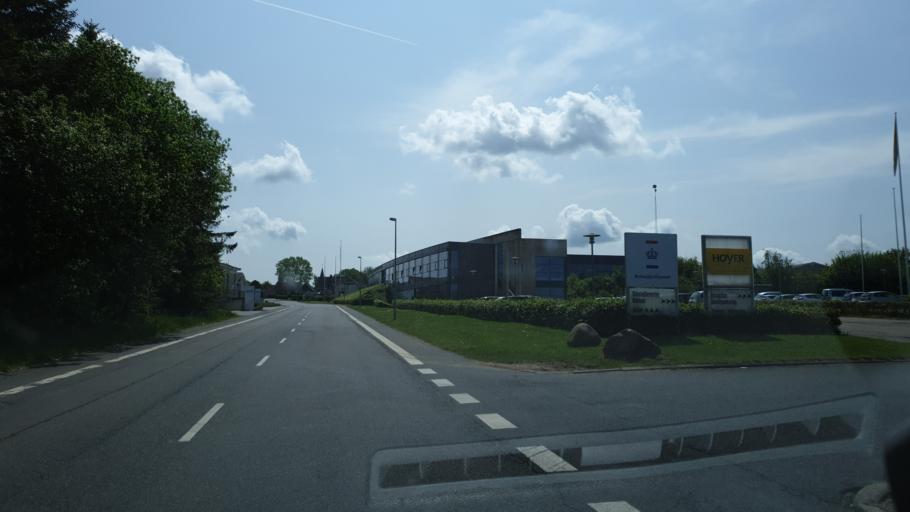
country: DK
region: Central Jutland
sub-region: Favrskov Kommune
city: Hadsten
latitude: 56.3152
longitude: 10.0410
